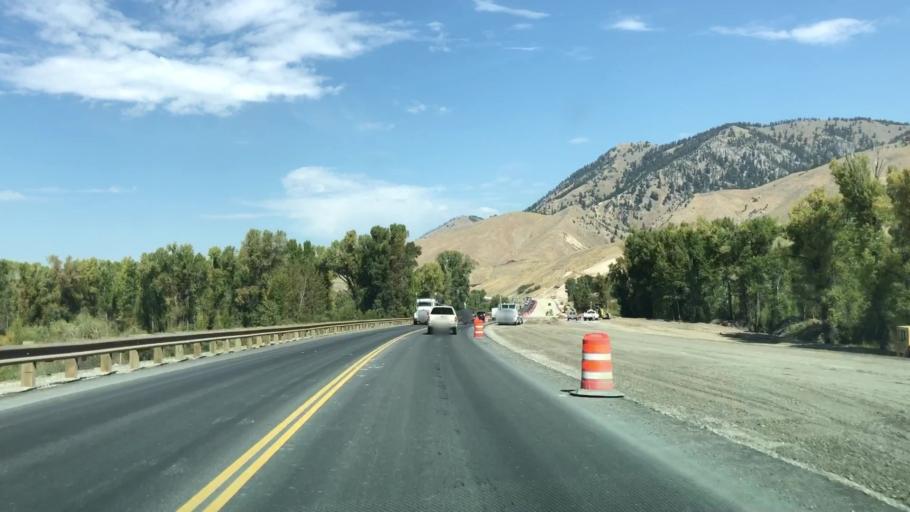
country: US
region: Wyoming
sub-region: Teton County
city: South Park
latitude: 43.3862
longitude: -110.7463
